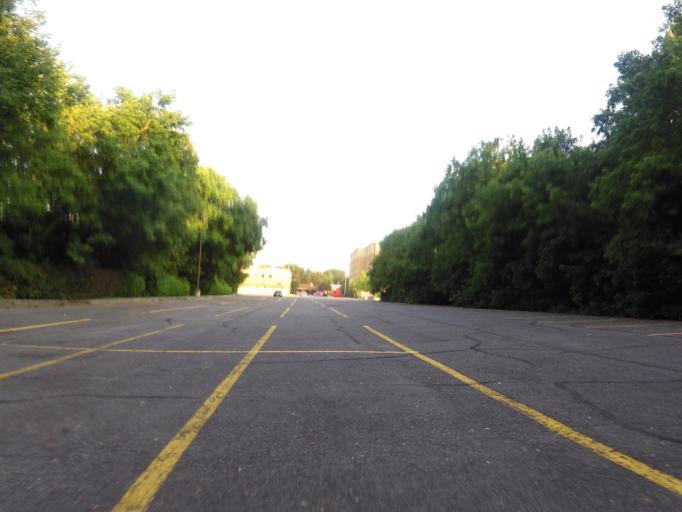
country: CA
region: Ontario
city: Bells Corners
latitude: 45.3251
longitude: -75.8315
